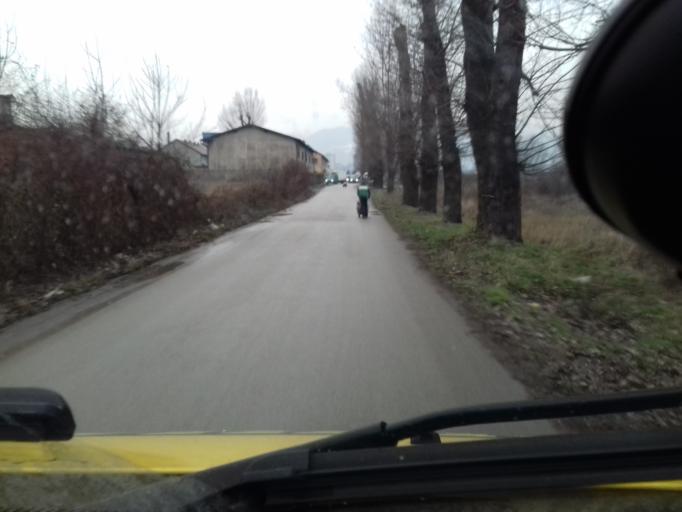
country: BA
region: Federation of Bosnia and Herzegovina
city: Zenica
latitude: 44.2212
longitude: 17.9090
